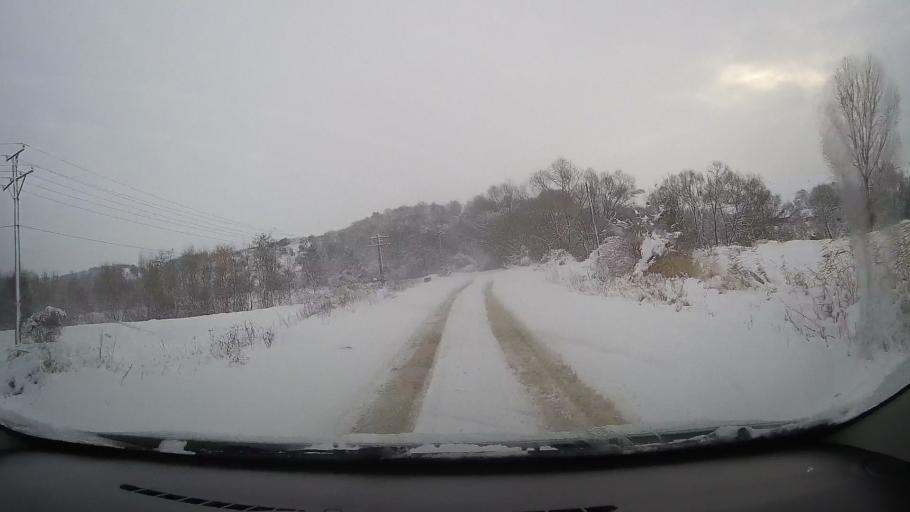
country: RO
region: Alba
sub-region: Comuna Pianu
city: Pianu de Jos
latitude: 45.9599
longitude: 23.4803
